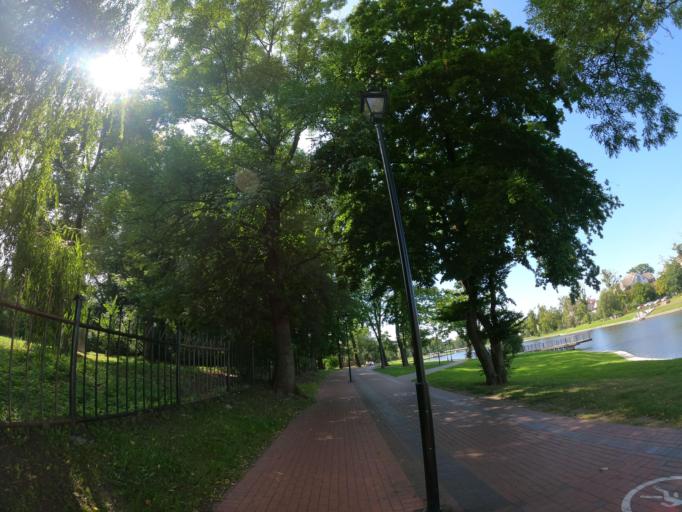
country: RU
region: Kaliningrad
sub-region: Gorod Kaliningrad
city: Kaliningrad
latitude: 54.7317
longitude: 20.5291
